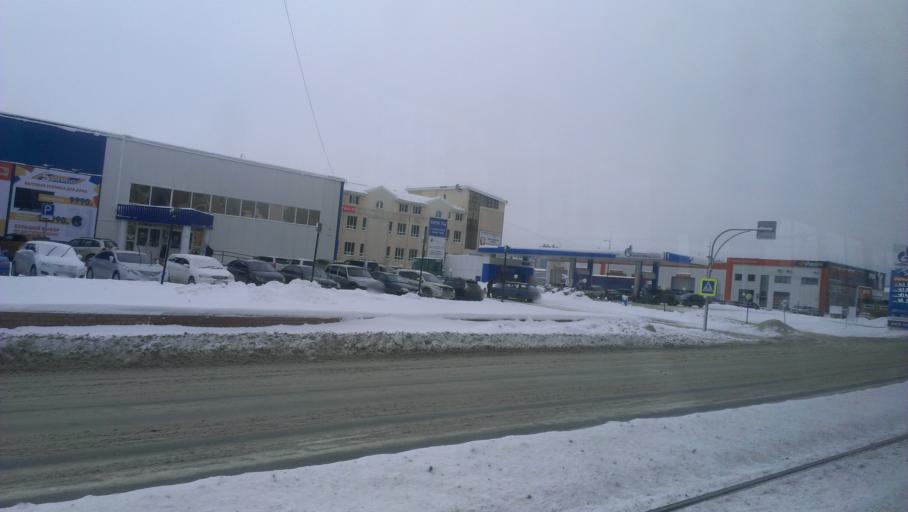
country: RU
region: Altai Krai
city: Novosilikatnyy
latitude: 53.3330
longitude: 83.6684
